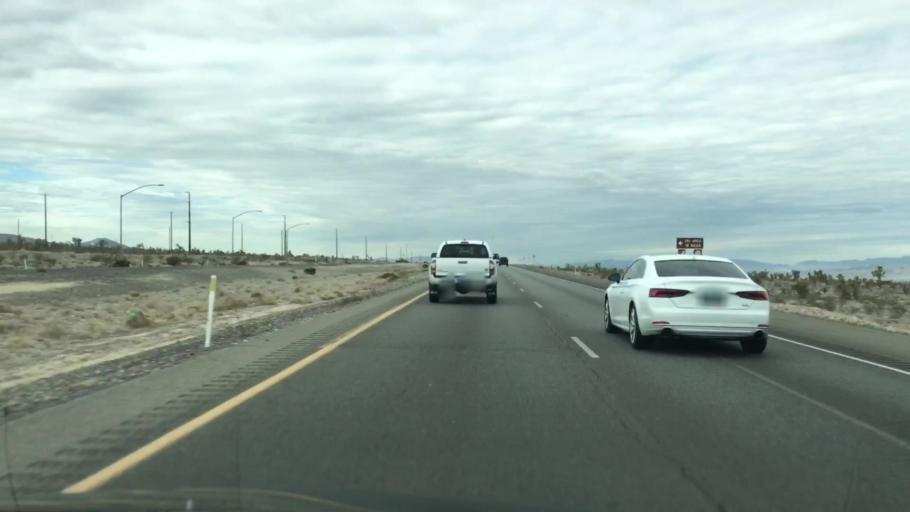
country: US
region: Nevada
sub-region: Clark County
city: Summerlin South
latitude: 36.4753
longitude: -115.4641
